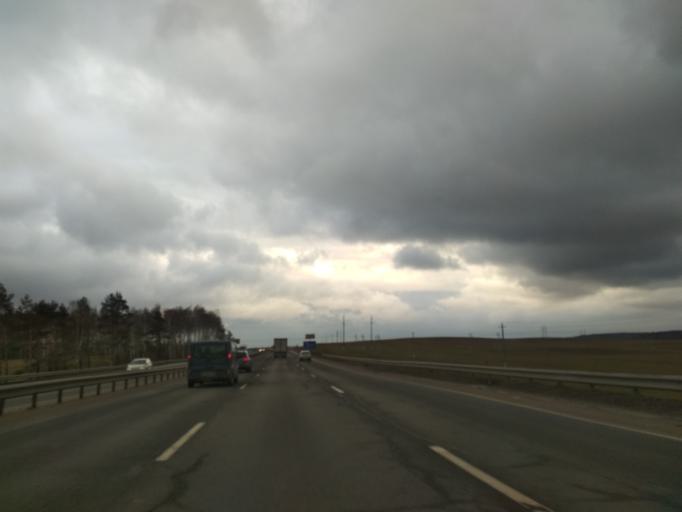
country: BY
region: Minsk
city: Pryvol'ny
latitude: 53.8170
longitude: 27.7692
